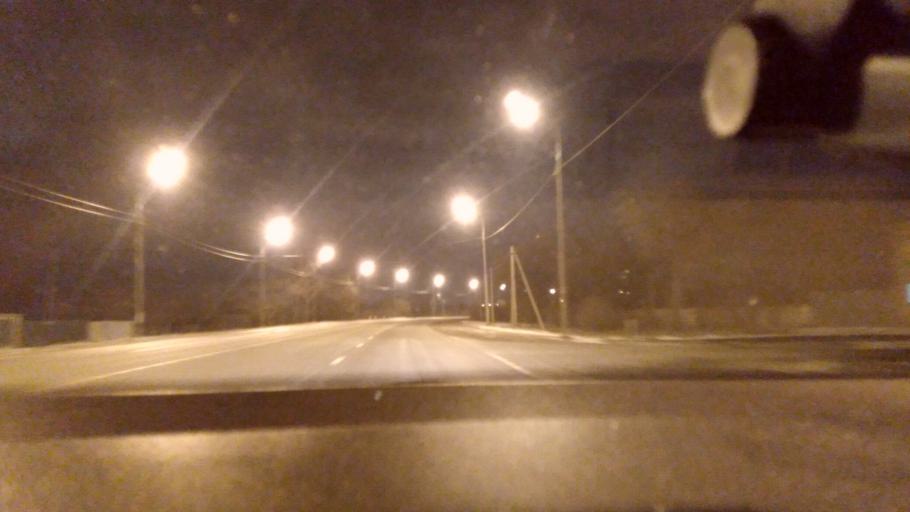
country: RU
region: Moskovskaya
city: Bronnitsy
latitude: 55.3925
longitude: 38.3258
